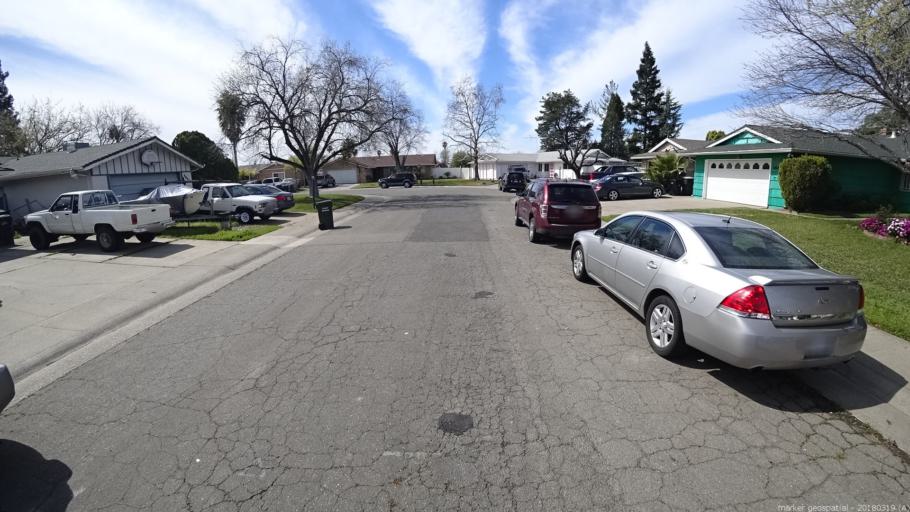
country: US
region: California
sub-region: Sacramento County
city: Parkway
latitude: 38.5052
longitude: -121.4516
